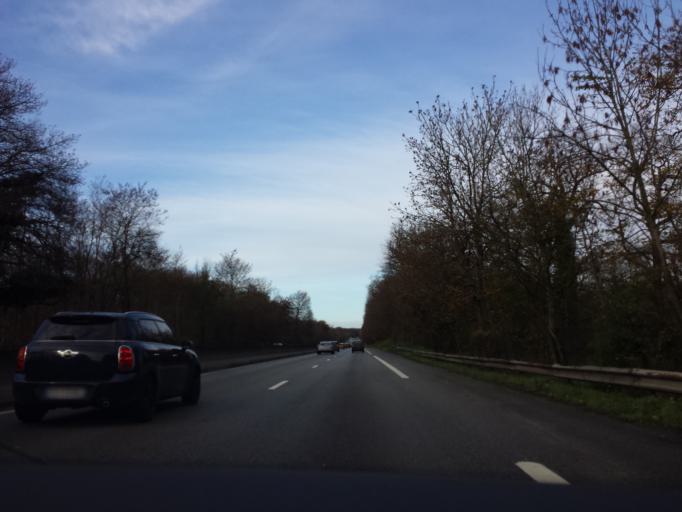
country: FR
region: Ile-de-France
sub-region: Departement des Yvelines
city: Noisy-le-Roi
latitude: 48.8600
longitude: 2.0485
